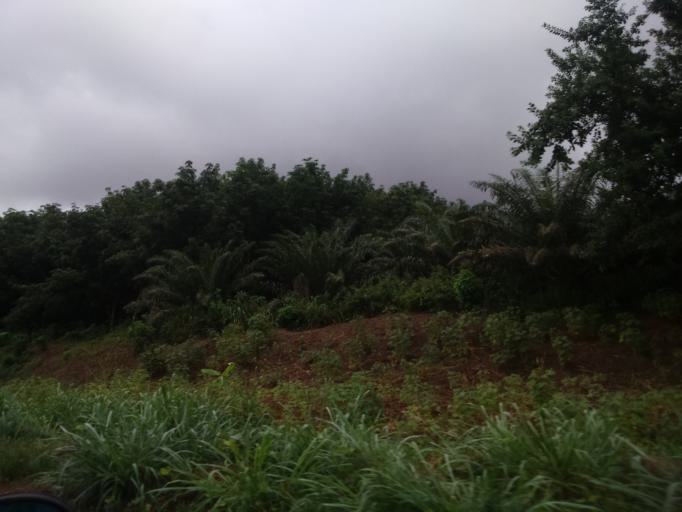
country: CI
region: Sud-Comoe
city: Adiake
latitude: 5.2993
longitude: -3.3421
